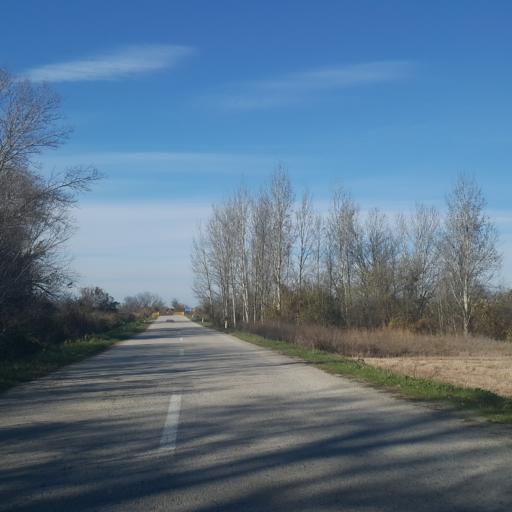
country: RS
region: Central Serbia
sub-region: Sumadijski Okrug
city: Topola
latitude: 44.2561
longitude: 20.8266
